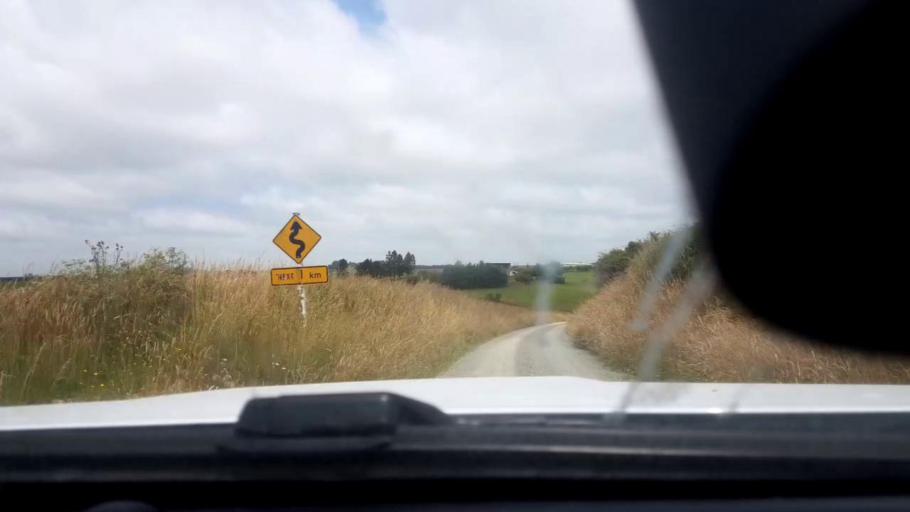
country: NZ
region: Canterbury
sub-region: Timaru District
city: Pleasant Point
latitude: -44.1586
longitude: 171.1474
